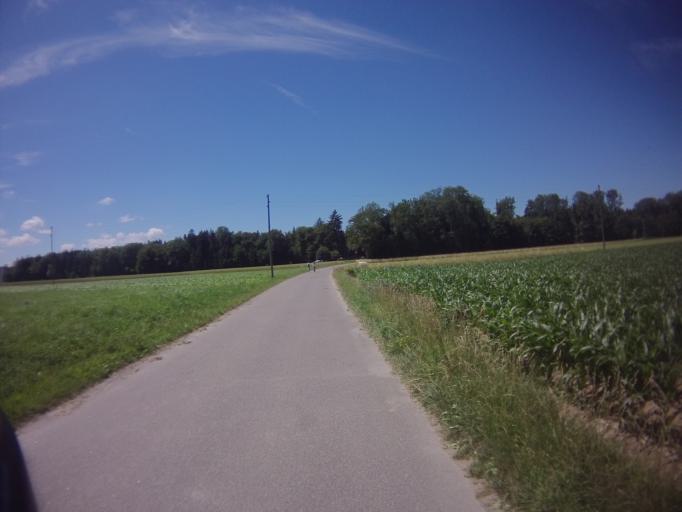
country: CH
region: Bern
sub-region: Emmental District
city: Kirchberg
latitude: 47.0797
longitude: 7.5664
